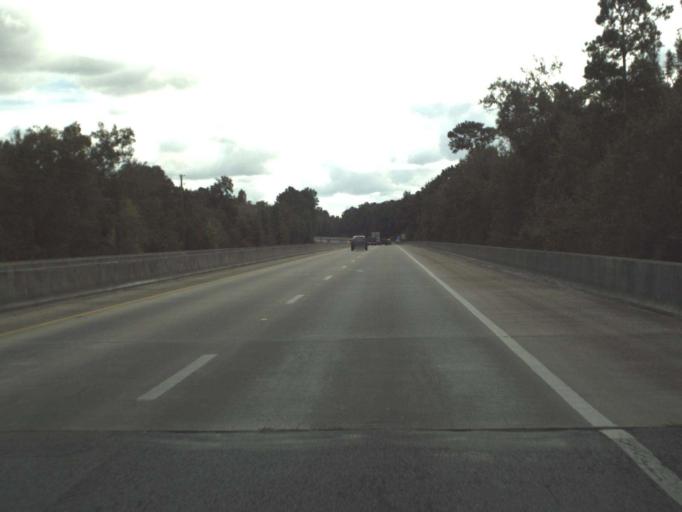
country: US
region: Florida
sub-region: Gadsden County
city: Havana
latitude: 30.5568
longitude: -84.3862
